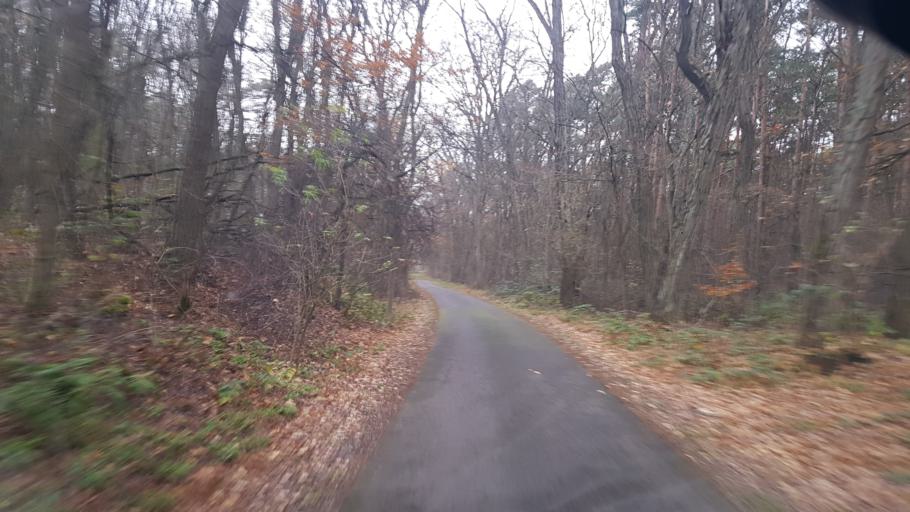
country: DE
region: Brandenburg
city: Schenkendobern
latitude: 51.9685
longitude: 14.6512
